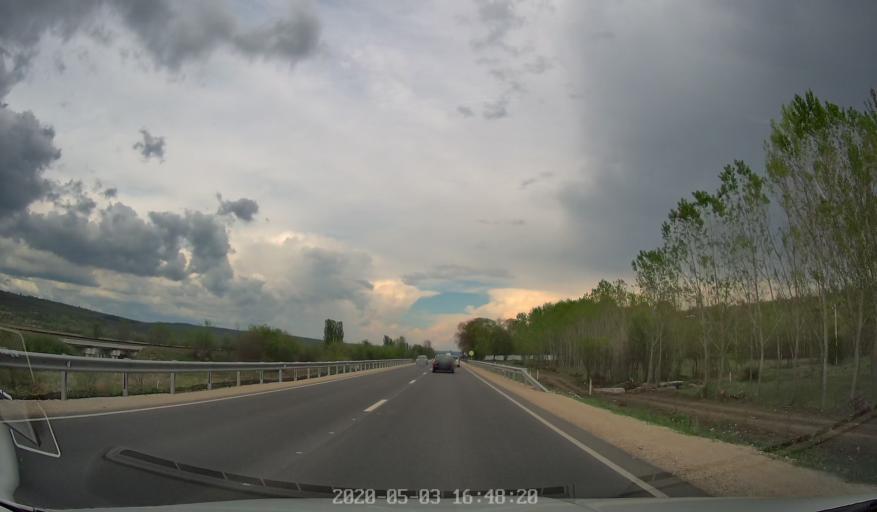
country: MD
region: Stinga Nistrului
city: Bucovat
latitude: 47.1773
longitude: 28.4924
